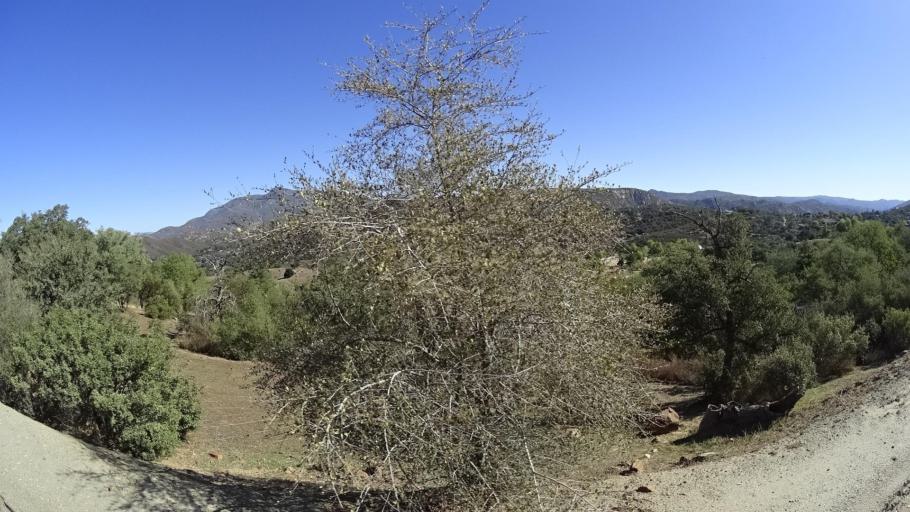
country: US
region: California
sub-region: San Diego County
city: Descanso
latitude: 32.8677
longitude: -116.6458
